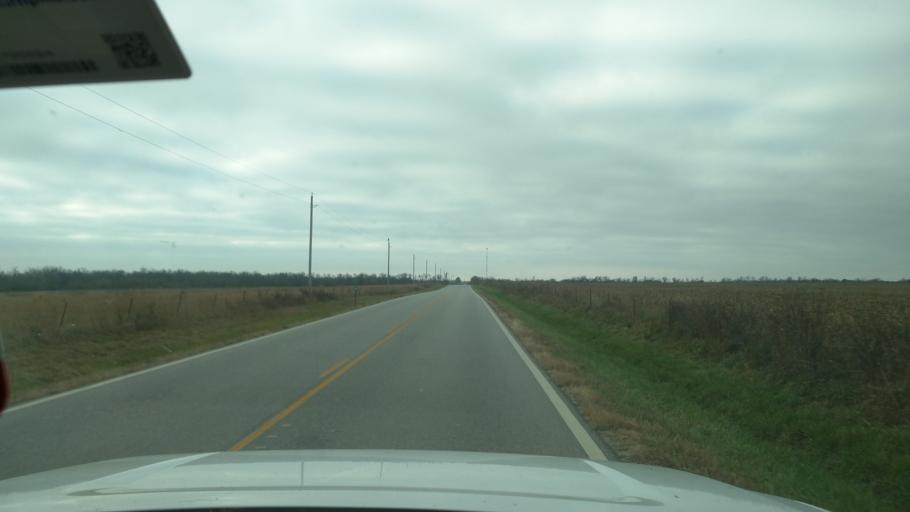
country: US
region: Kansas
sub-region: Elk County
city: Howard
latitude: 37.6486
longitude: -96.2346
